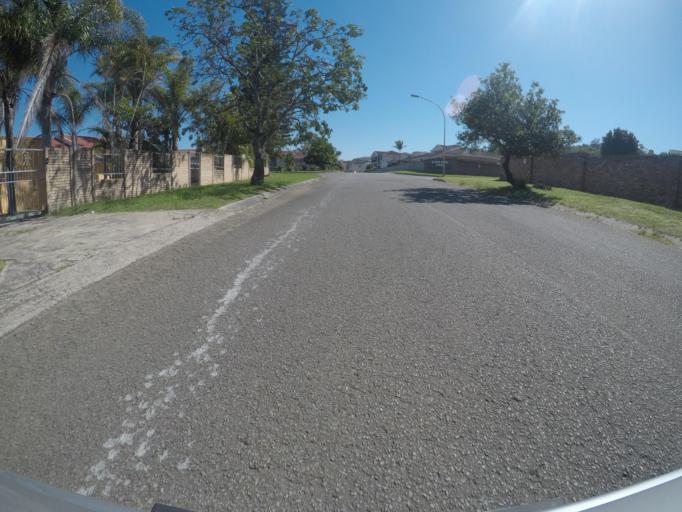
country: ZA
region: Eastern Cape
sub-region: Buffalo City Metropolitan Municipality
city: East London
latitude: -32.9556
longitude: 27.9118
